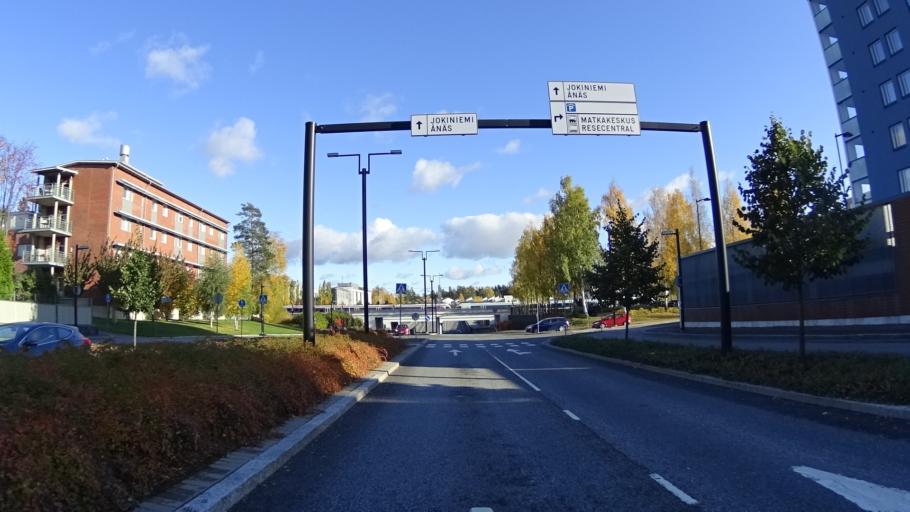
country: FI
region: Uusimaa
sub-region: Helsinki
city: Vantaa
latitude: 60.2992
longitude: 25.0437
